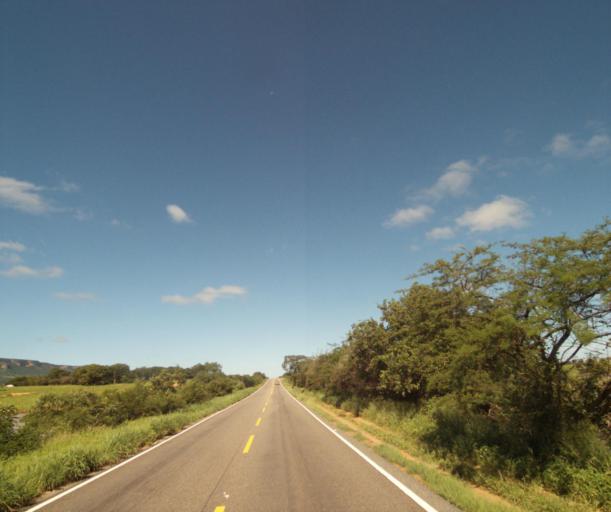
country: BR
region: Bahia
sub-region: Palmas De Monte Alto
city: Palmas de Monte Alto
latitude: -14.2435
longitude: -43.0876
